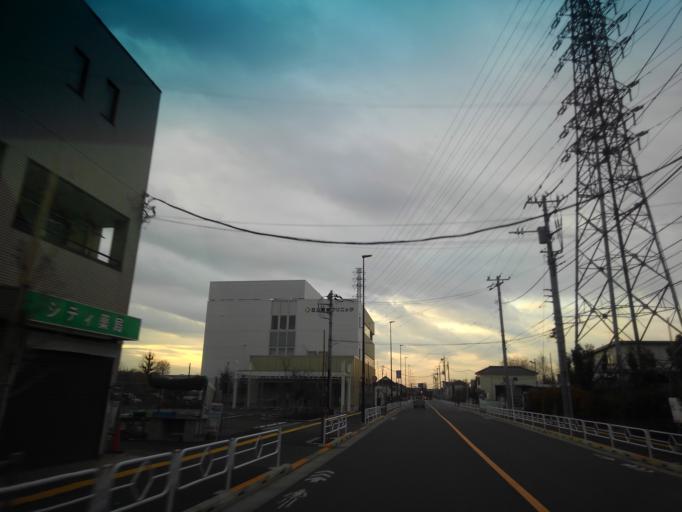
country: JP
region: Tokyo
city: Kokubunji
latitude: 35.7217
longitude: 139.4427
